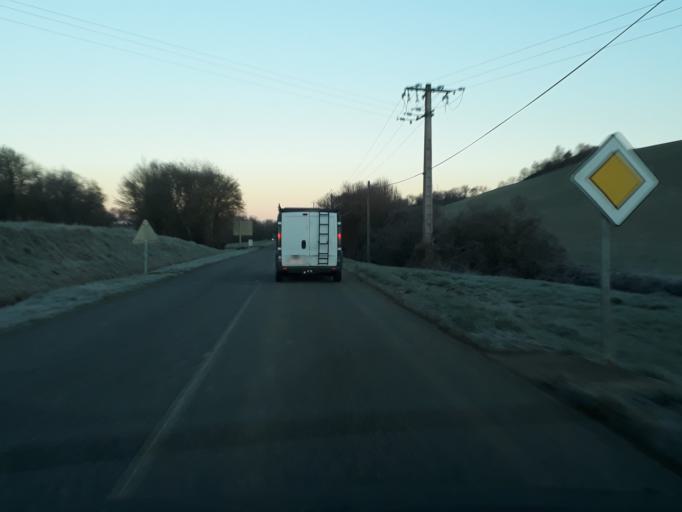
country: FR
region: Midi-Pyrenees
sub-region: Departement du Gers
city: Aubiet
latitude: 43.5597
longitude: 0.7946
